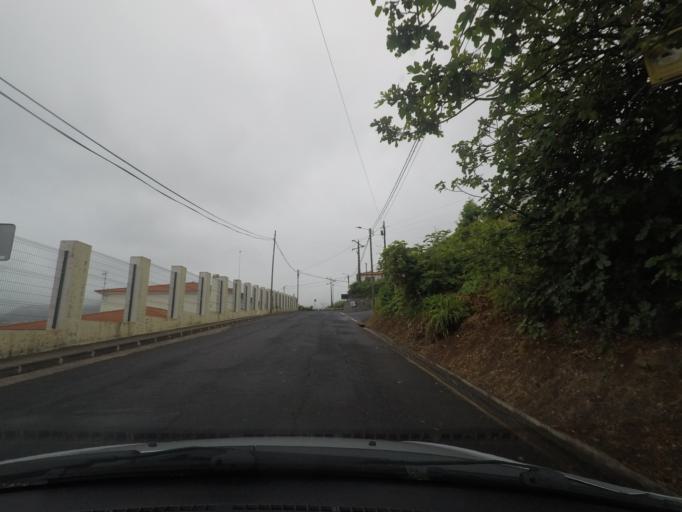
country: PT
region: Madeira
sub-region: Santana
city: Santana
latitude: 32.7878
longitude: -16.8553
